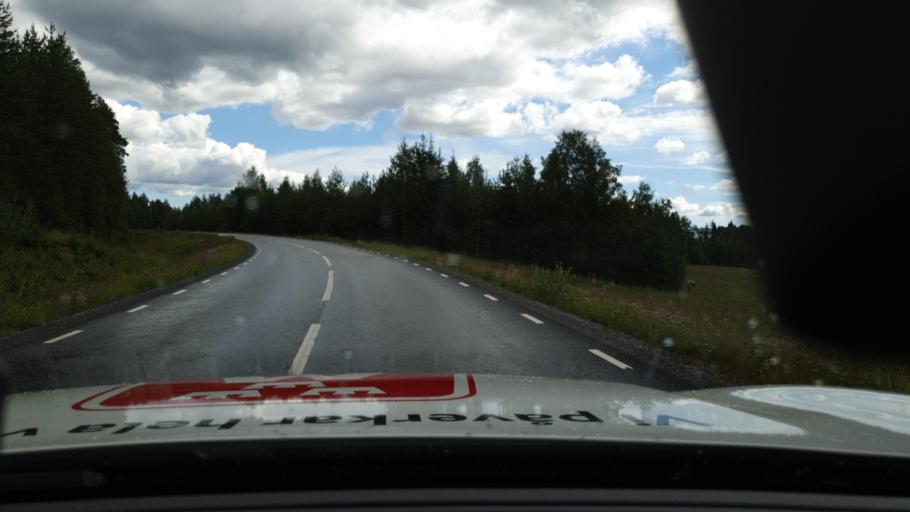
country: SE
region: Norrbotten
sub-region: Bodens Kommun
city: Saevast
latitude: 65.8383
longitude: 21.8308
